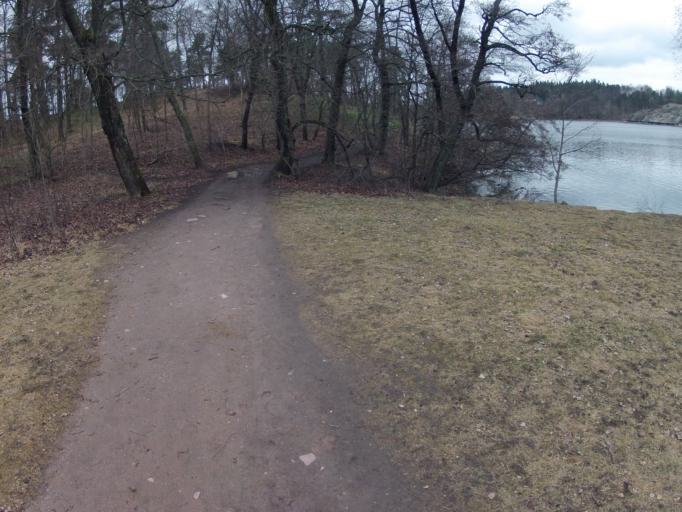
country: SE
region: Stockholm
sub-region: Norrtalje Kommun
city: Bergshamra
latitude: 59.3748
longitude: 18.0211
